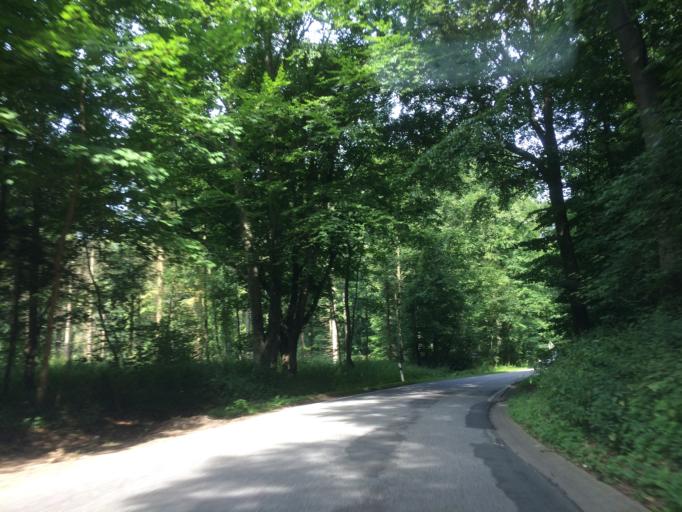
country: DE
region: Schleswig-Holstein
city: Altenhof
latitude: 54.4417
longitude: 9.8637
